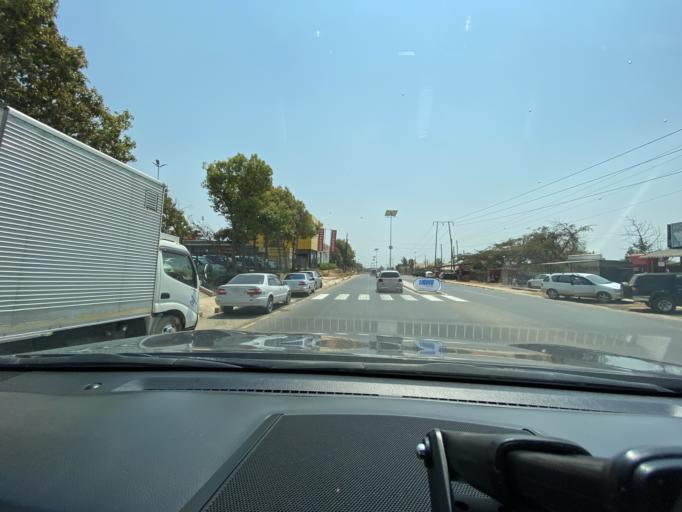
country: ZM
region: Lusaka
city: Lusaka
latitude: -15.3719
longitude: 28.3457
